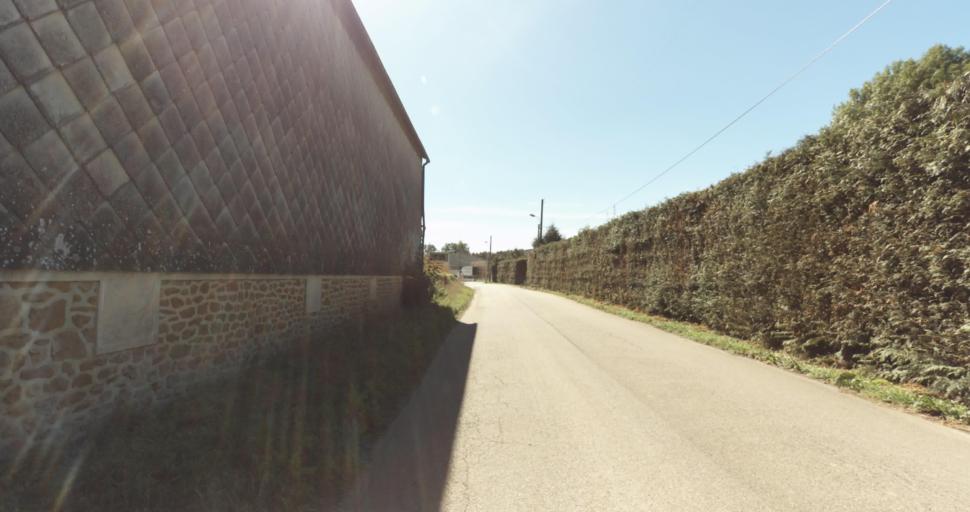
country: FR
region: Lower Normandy
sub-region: Departement de l'Orne
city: Gace
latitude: 48.7894
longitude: 0.2912
